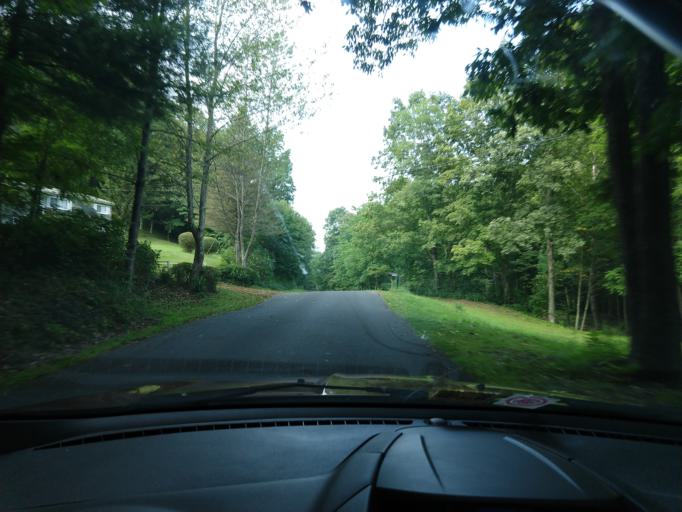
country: US
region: Virginia
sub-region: City of Covington
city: Covington
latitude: 37.8926
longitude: -80.0916
